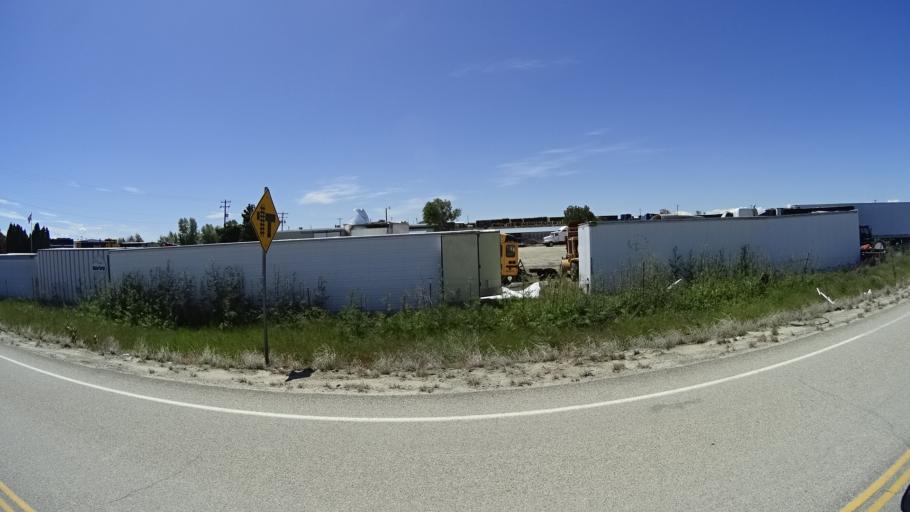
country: US
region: Idaho
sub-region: Ada County
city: Boise
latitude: 43.5605
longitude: -116.1743
